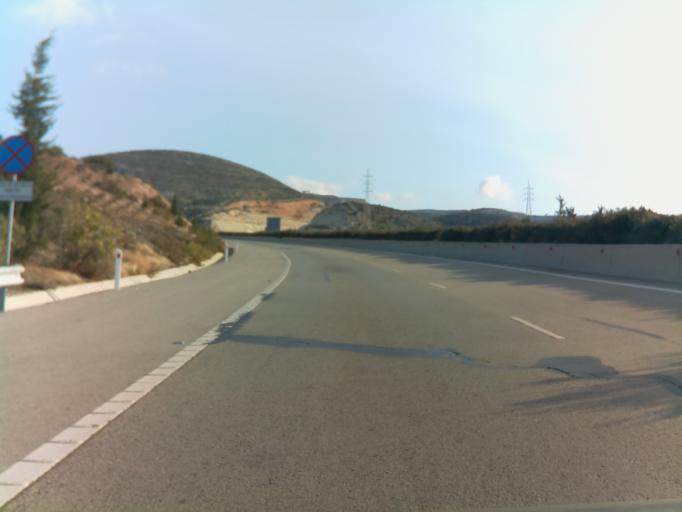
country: CY
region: Limassol
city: Pissouri
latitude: 34.6696
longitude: 32.6237
